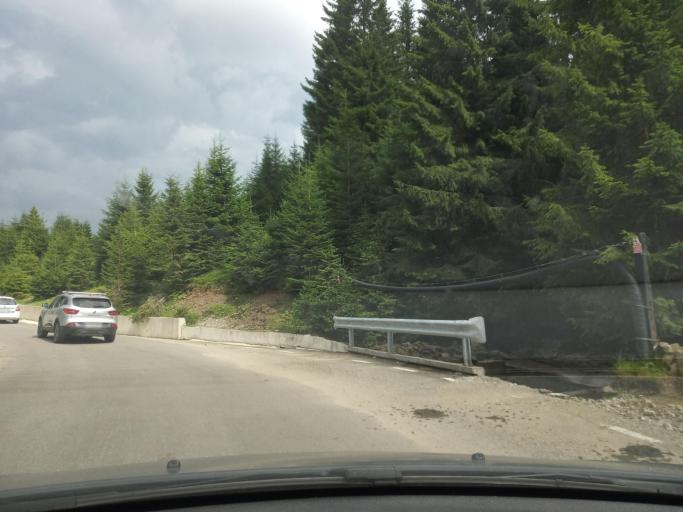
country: RO
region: Dambovita
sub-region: Comuna Moroeni
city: Glod
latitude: 45.3247
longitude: 25.4595
